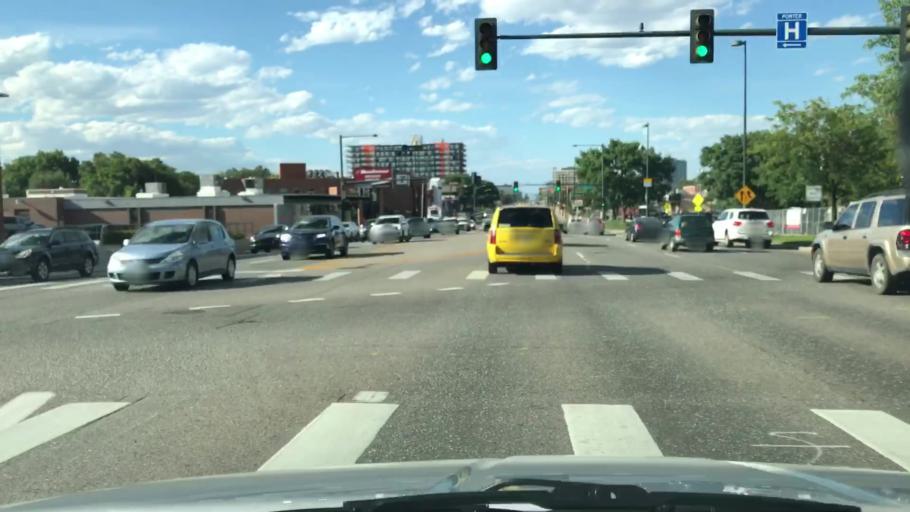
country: US
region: Colorado
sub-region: Arapahoe County
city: Cherry Hills Village
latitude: 39.6675
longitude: -104.9406
